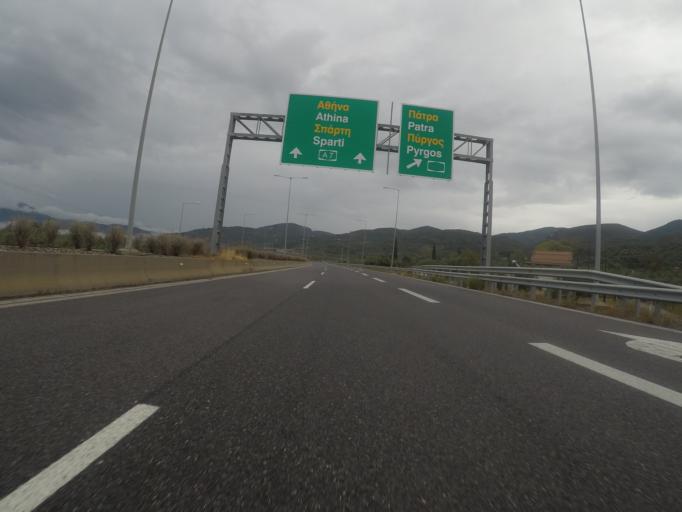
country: GR
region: Peloponnese
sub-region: Nomos Messinias
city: Meligalas
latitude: 37.2444
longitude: 22.0204
